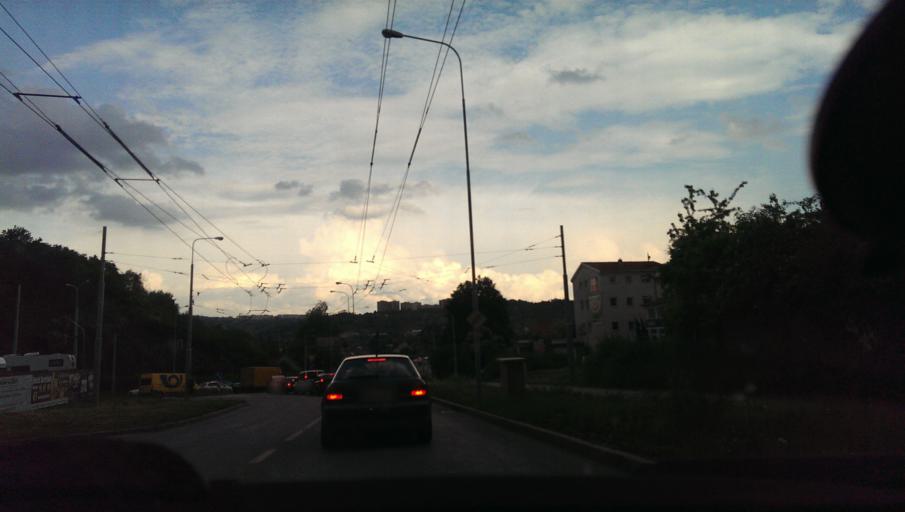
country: CZ
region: South Moravian
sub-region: Mesto Brno
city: Brno
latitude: 49.2145
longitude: 16.6327
